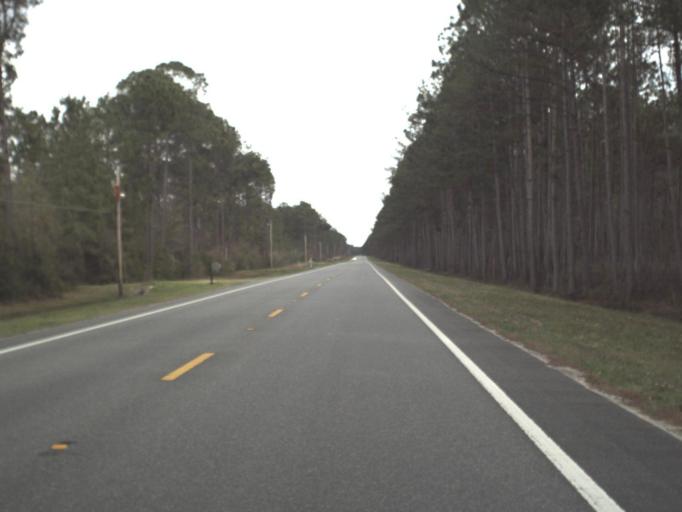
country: US
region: Florida
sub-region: Gadsden County
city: Midway
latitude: 30.3887
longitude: -84.6053
